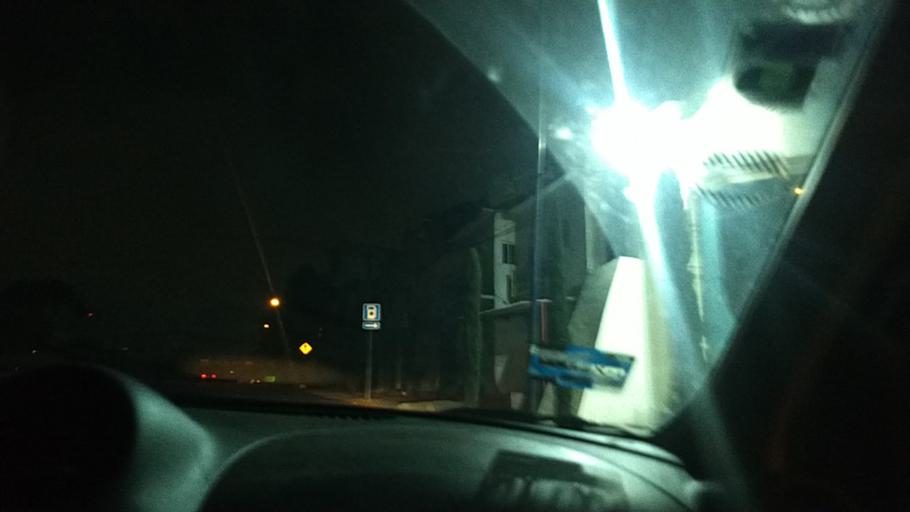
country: MX
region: Mexico
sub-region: Tultitlan
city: Buenavista
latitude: 19.5890
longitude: -99.1920
